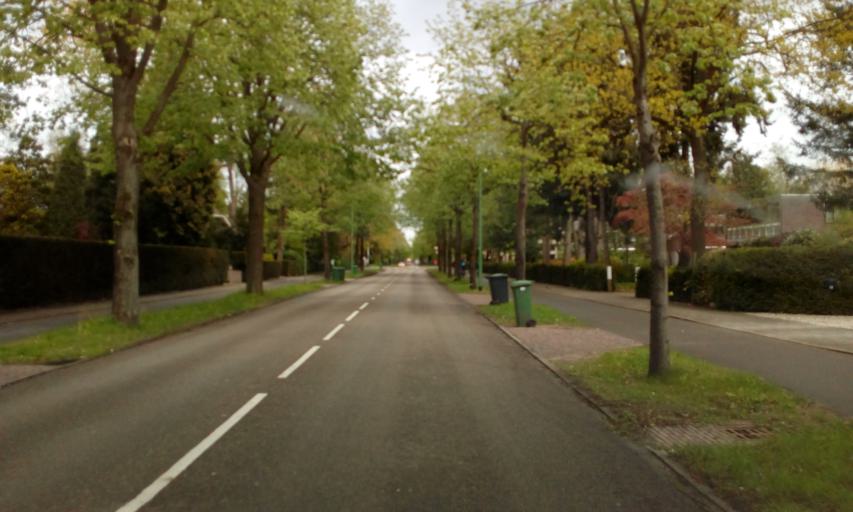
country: NL
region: Utrecht
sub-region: Gemeente Zeist
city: Zeist
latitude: 52.0955
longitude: 5.2530
